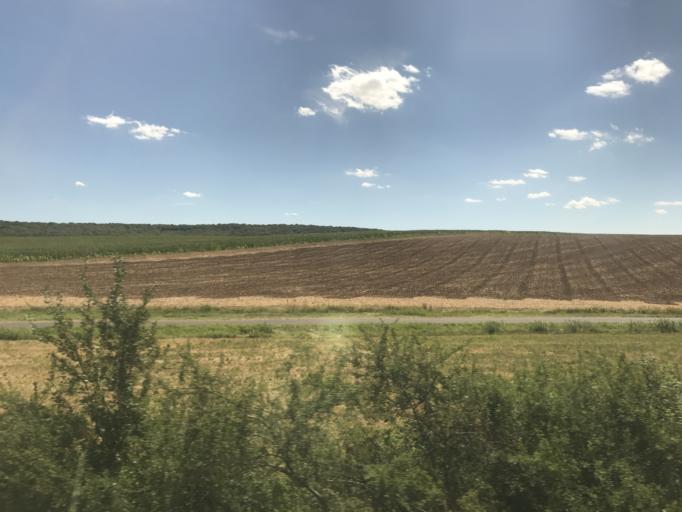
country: FR
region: Lorraine
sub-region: Departement de la Moselle
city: Remilly
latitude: 48.9631
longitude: 6.4869
